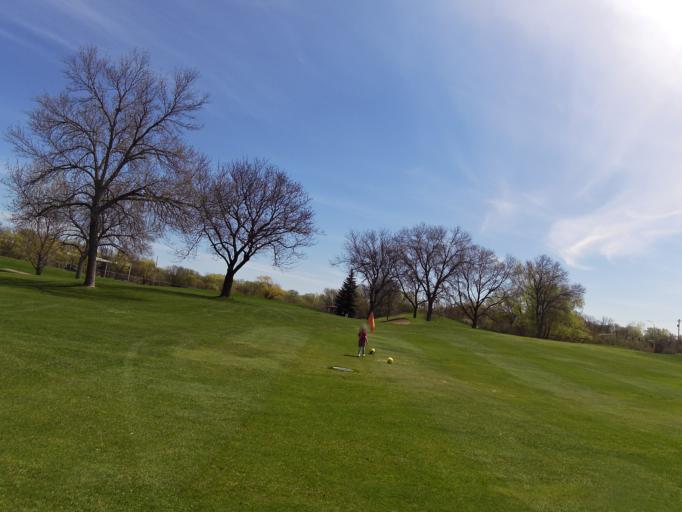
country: US
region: Minnesota
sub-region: Scott County
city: Savage
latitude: 44.8200
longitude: -93.3524
